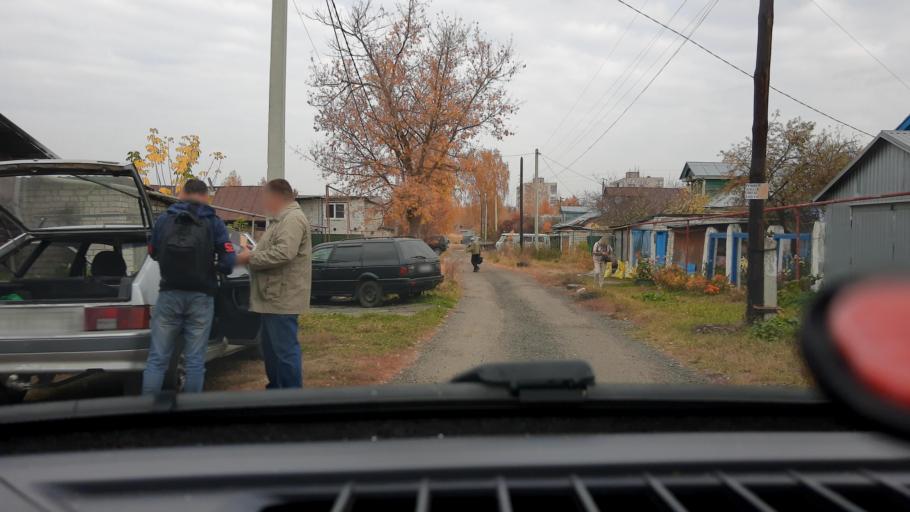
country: RU
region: Nizjnij Novgorod
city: Gorbatovka
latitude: 56.3292
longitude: 43.8346
